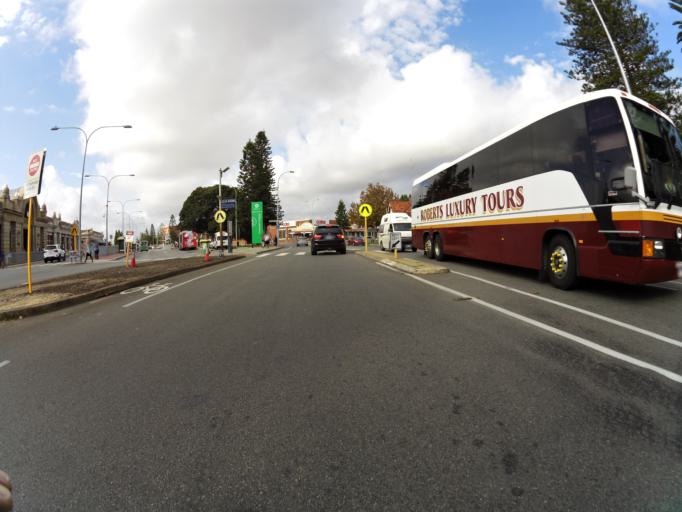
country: AU
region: Western Australia
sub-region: Fremantle
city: South Fremantle
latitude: -32.0525
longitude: 115.7451
